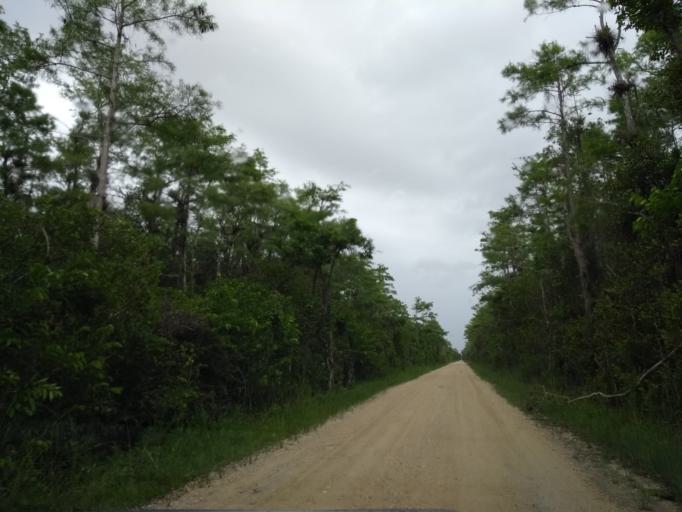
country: US
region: Florida
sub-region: Miami-Dade County
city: The Hammocks
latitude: 25.7522
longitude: -80.9713
